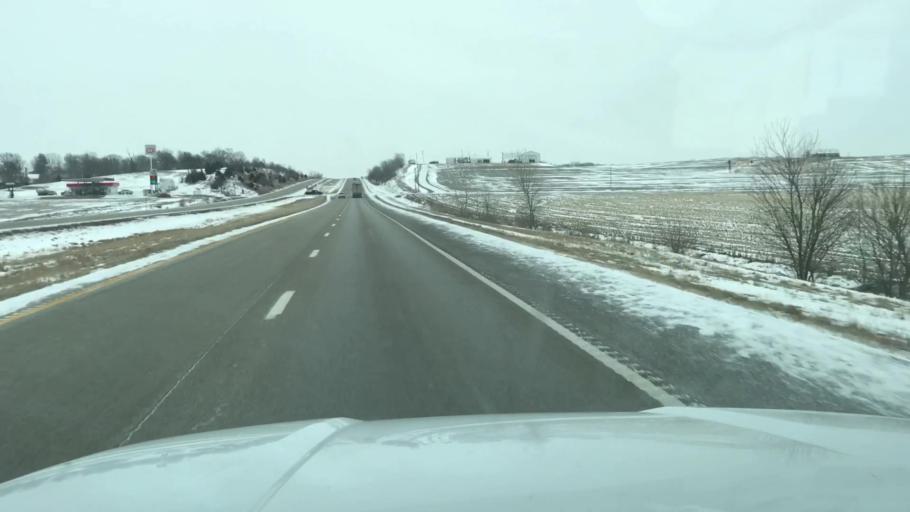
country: US
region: Missouri
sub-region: Buchanan County
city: Saint Joseph
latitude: 39.7475
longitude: -94.7152
